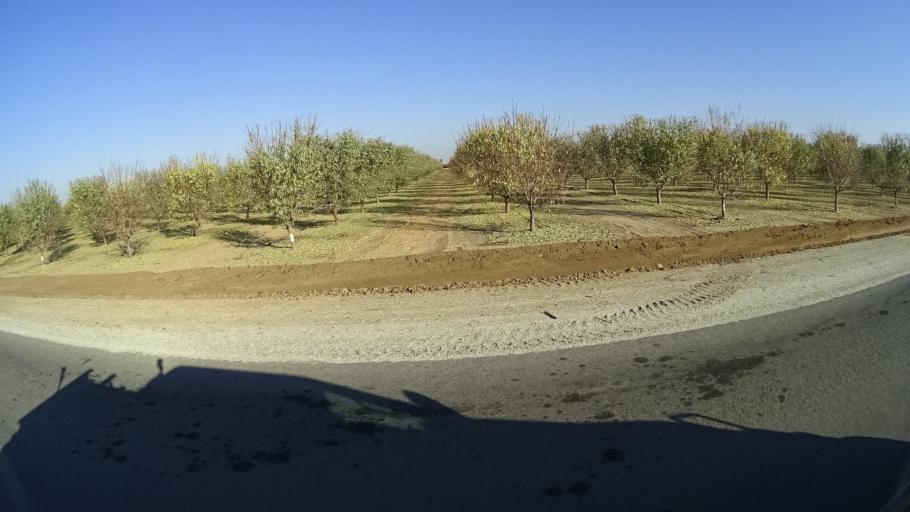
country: US
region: California
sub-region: Tulare County
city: Richgrove
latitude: 35.7688
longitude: -119.1706
